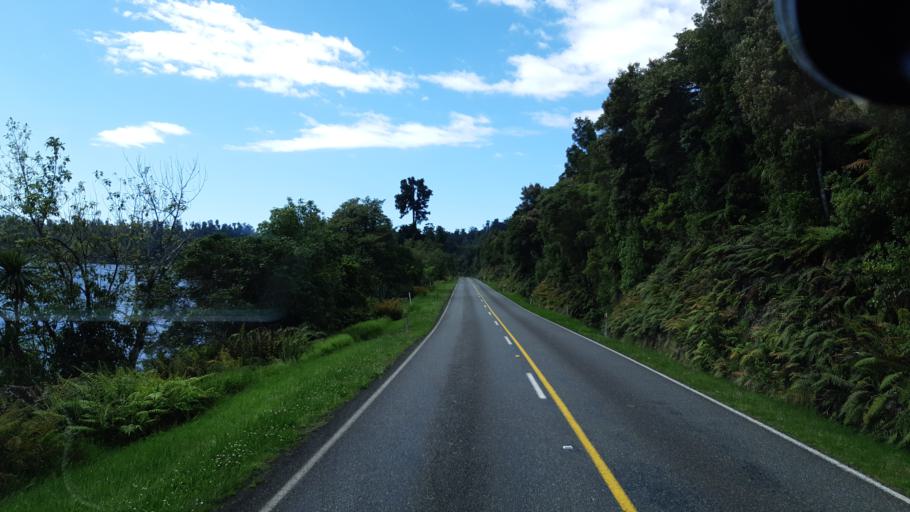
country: NZ
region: West Coast
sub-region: Westland District
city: Hokitika
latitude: -43.0572
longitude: 170.6360
